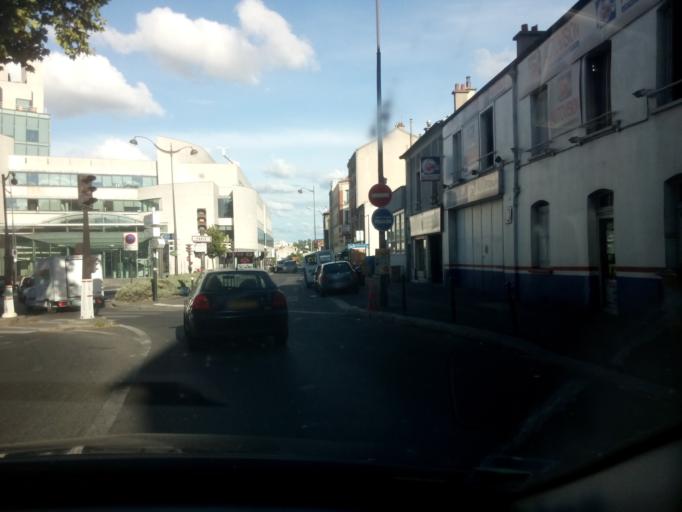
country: FR
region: Ile-de-France
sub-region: Departement du Val-de-Marne
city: Gentilly
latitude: 48.8159
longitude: 2.3434
